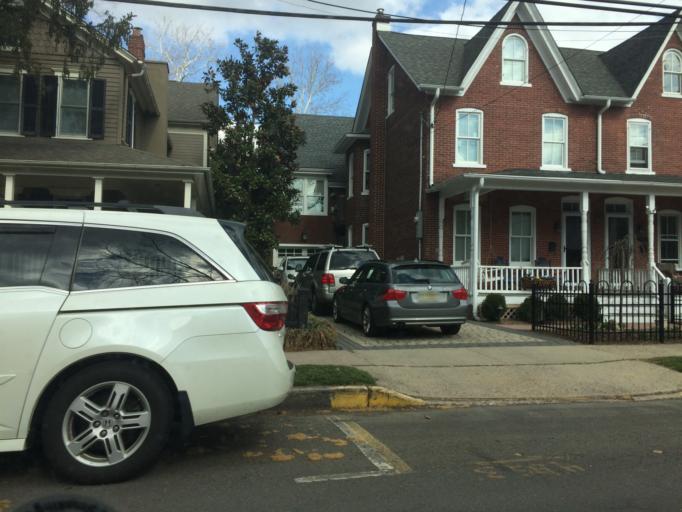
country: US
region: Pennsylvania
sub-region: Bucks County
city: New Hope
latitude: 40.3663
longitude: -74.9522
